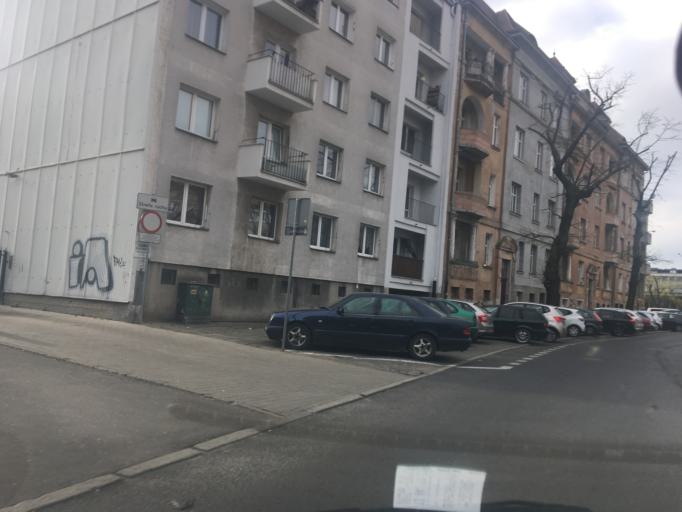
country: PL
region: Greater Poland Voivodeship
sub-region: Poznan
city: Poznan
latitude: 52.4003
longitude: 16.9332
